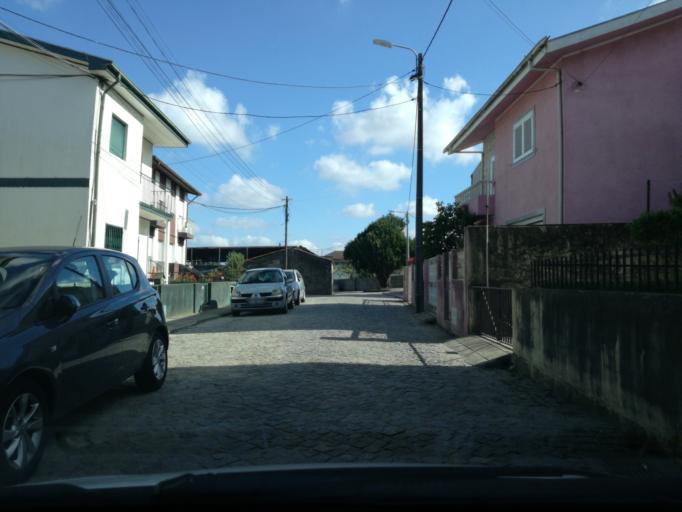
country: PT
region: Porto
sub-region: Valongo
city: Ermesinde
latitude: 41.2309
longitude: -8.5609
